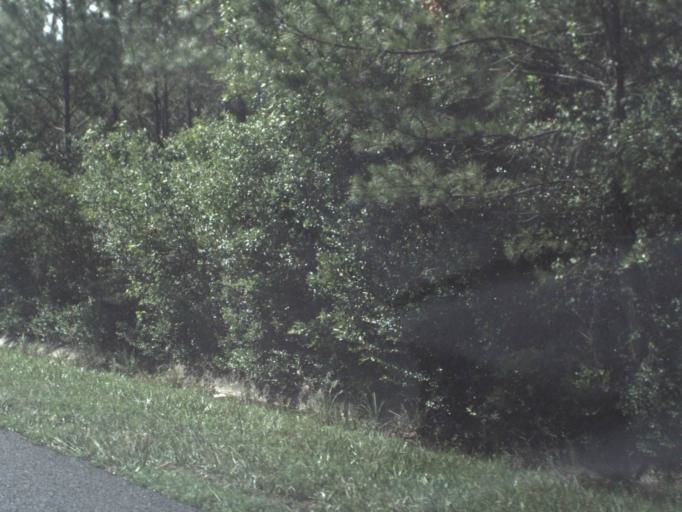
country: US
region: Florida
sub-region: Nassau County
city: Hilliard
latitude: 30.6702
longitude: -81.8959
